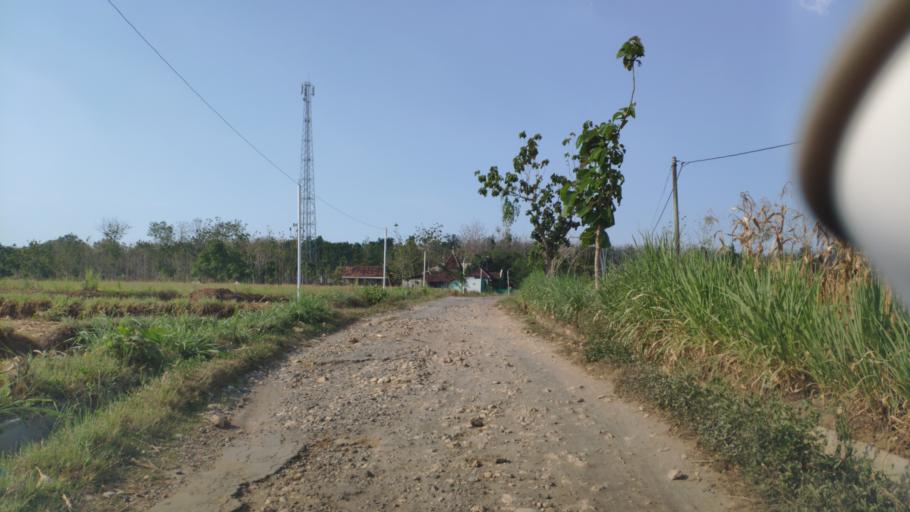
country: ID
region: Central Java
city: Ngapus
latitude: -6.9779
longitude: 111.1589
